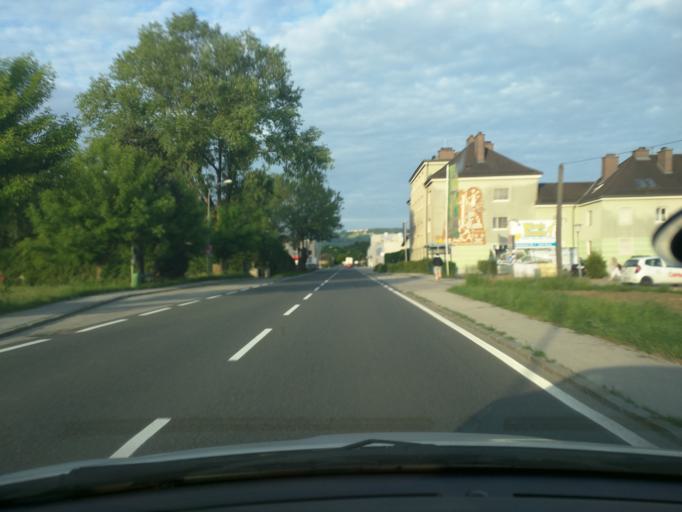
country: AT
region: Lower Austria
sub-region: Politischer Bezirk Amstetten
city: Kematen an der Ybbs
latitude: 48.0191
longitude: 14.7524
